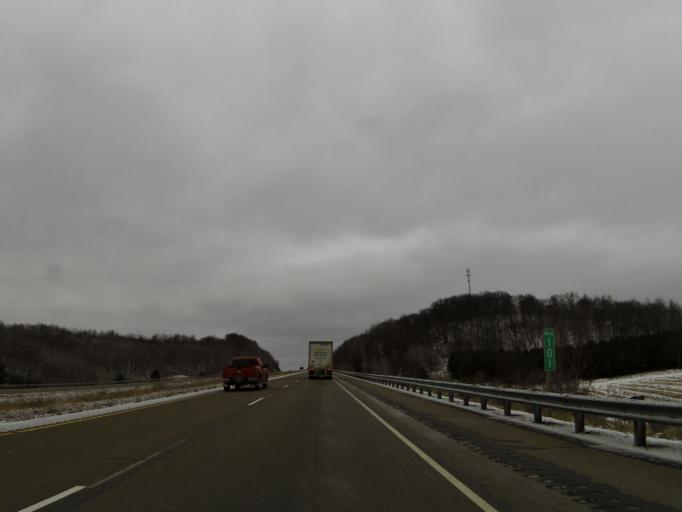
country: US
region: Wisconsin
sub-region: Trempealeau County
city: Osseo
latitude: 44.4314
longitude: -91.0666
